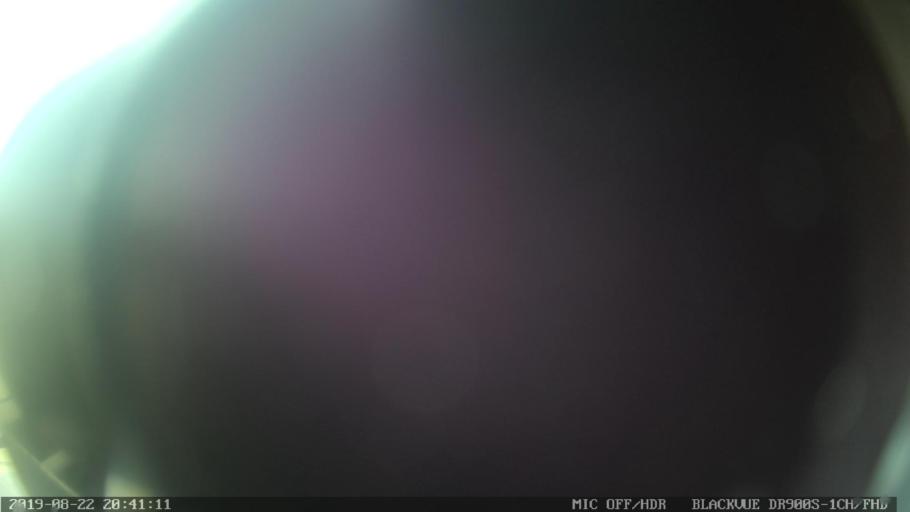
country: PT
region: Castelo Branco
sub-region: Proenca-A-Nova
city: Proenca-a-Nova
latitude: 39.6857
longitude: -7.8004
